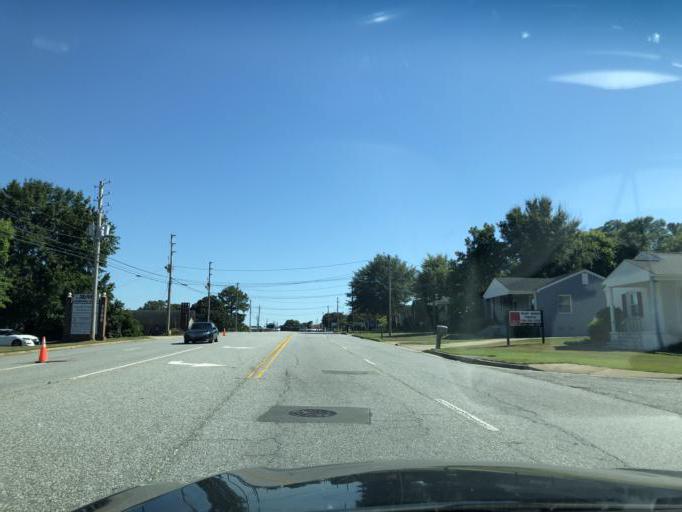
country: US
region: Georgia
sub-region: Muscogee County
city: Columbus
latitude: 32.5112
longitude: -84.9538
